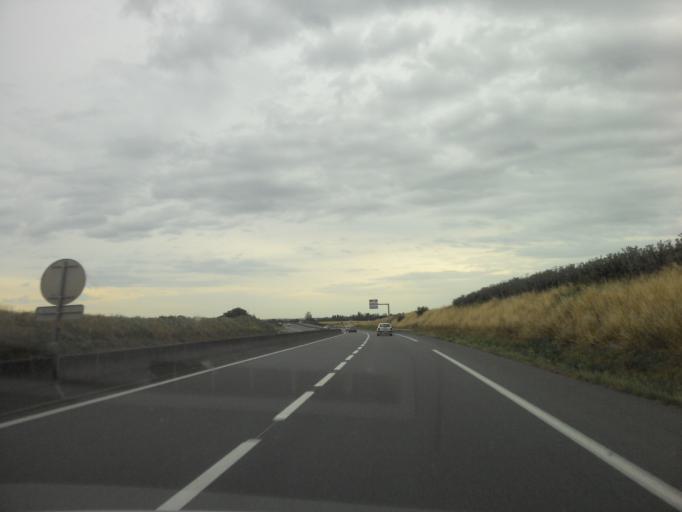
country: FR
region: Auvergne
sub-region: Departement du Puy-de-Dome
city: Menetrol
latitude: 45.8850
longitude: 3.1353
